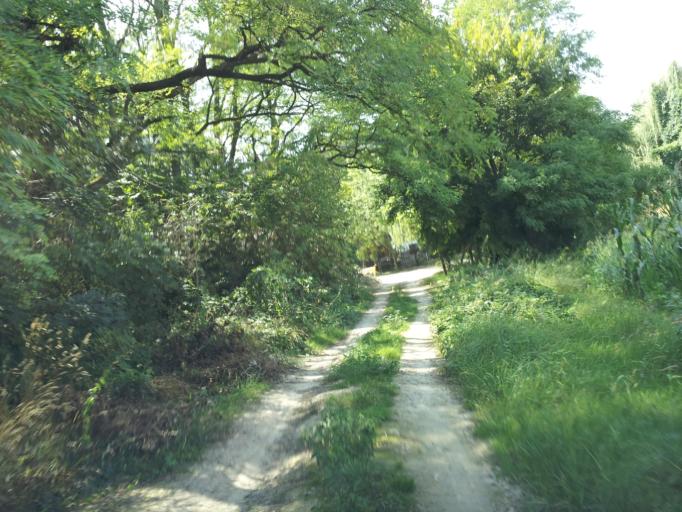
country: HU
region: Pest
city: Szigetszentmiklos
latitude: 47.3309
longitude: 19.0503
